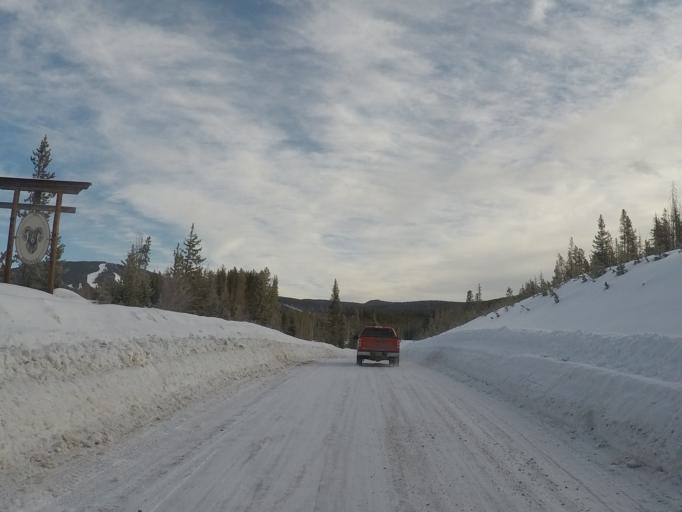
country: US
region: Montana
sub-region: Granite County
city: Philipsburg
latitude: 46.2276
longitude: -113.2498
